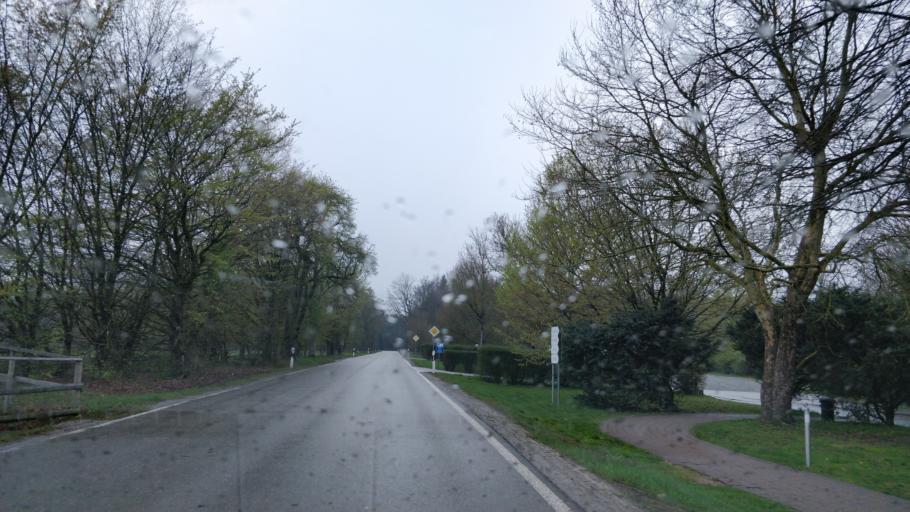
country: DE
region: Baden-Wuerttemberg
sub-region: Regierungsbezirk Stuttgart
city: Oberrot
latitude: 49.0410
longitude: 9.6103
